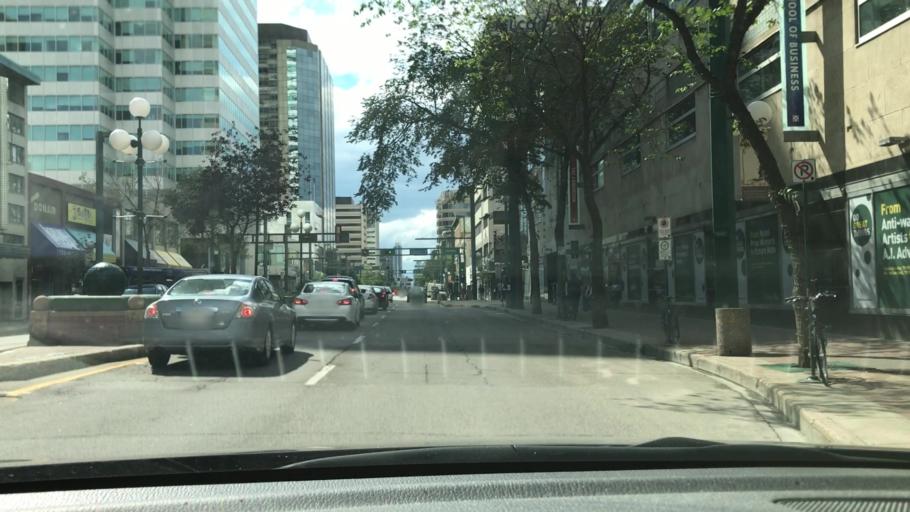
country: CA
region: Alberta
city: Edmonton
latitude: 53.5410
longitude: -113.4959
